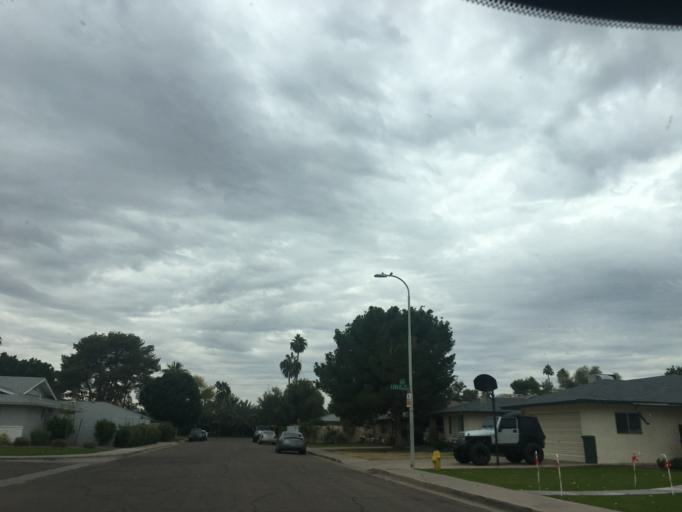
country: US
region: Arizona
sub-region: Maricopa County
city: Guadalupe
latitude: 33.3684
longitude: -111.9259
